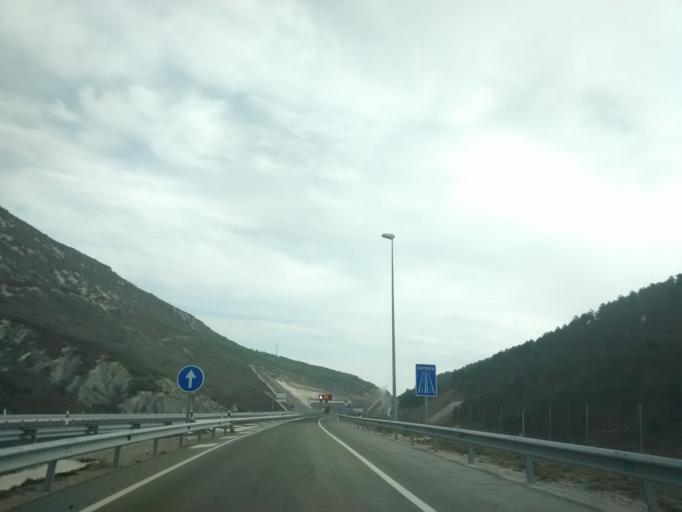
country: ES
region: Navarre
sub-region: Provincia de Navarra
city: Liedena
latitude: 42.6239
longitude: -1.2651
